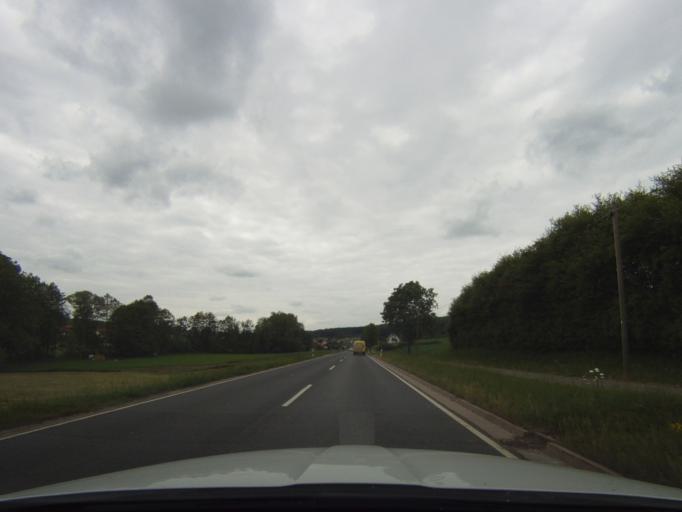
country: DE
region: Bavaria
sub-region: Upper Franconia
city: Michelau
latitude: 50.1207
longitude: 11.1038
